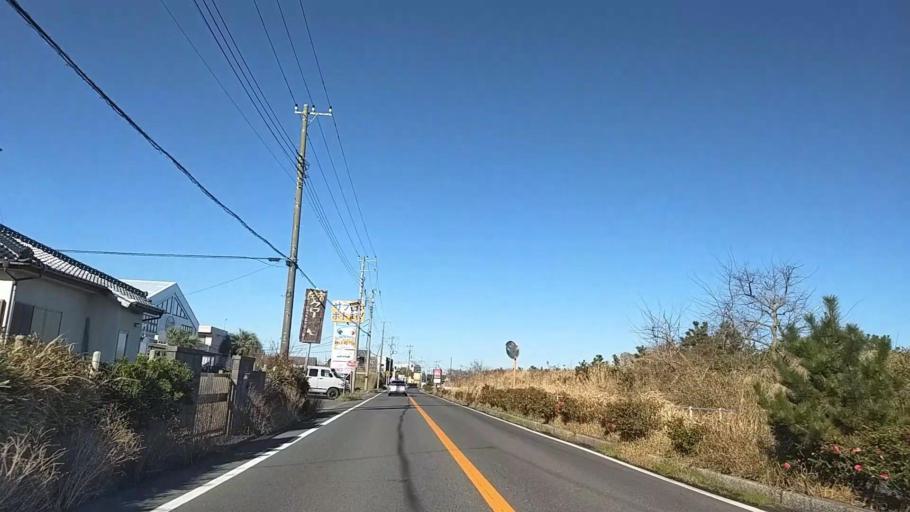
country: JP
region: Chiba
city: Ohara
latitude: 35.3436
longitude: 140.3903
